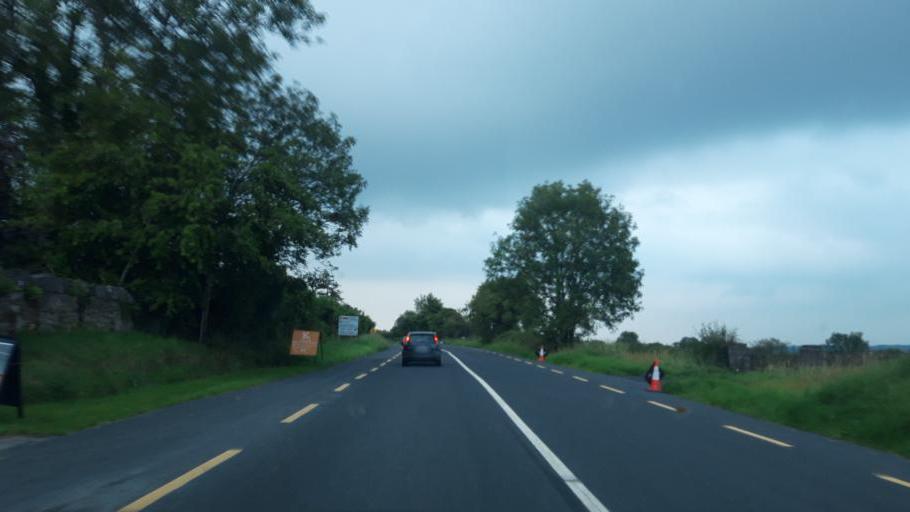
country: IE
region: Leinster
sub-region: Kilkenny
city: Thomastown
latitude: 52.5534
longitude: -7.1270
